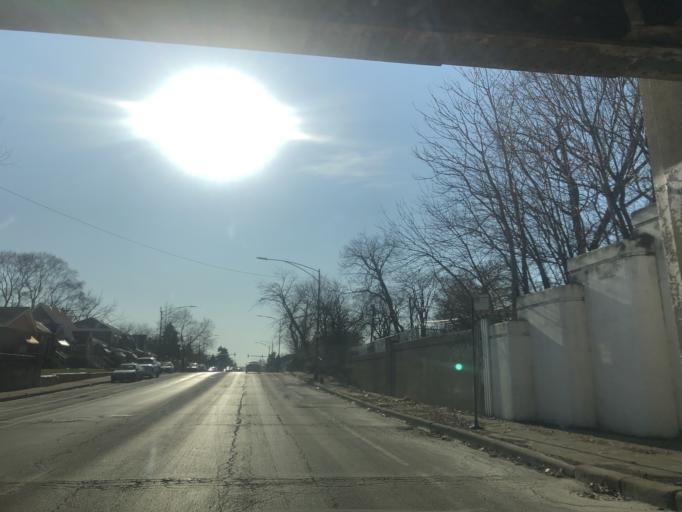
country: US
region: Illinois
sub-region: Cook County
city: Evergreen Park
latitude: 41.7578
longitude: -87.6733
